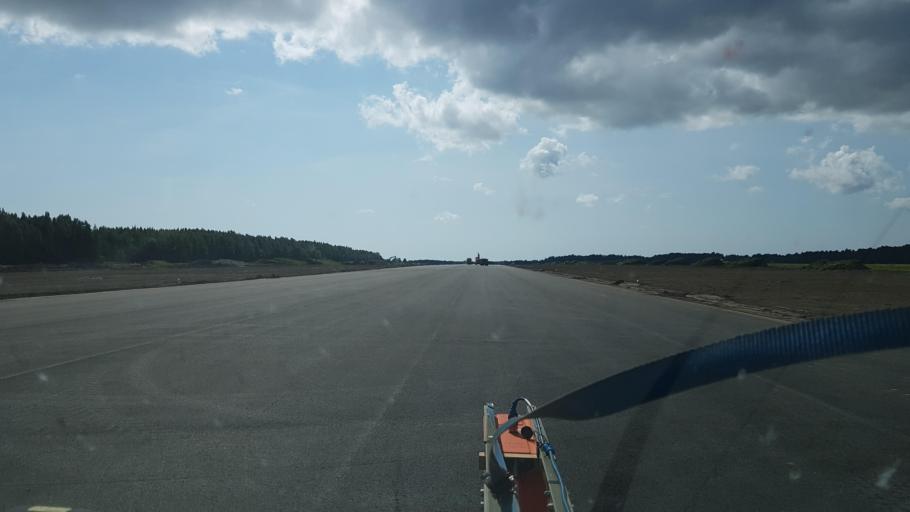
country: EE
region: Paernumaa
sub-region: Sauga vald
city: Sauga
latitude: 58.4225
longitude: 24.4777
